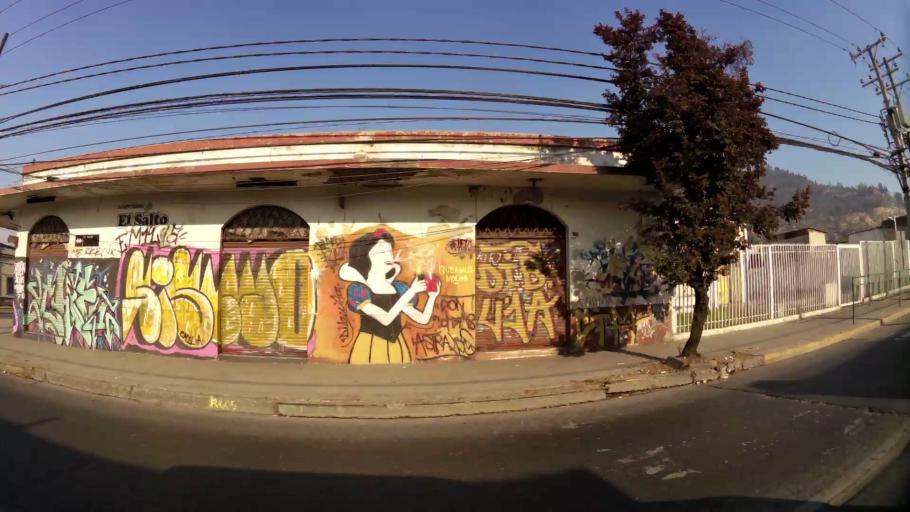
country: CL
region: Santiago Metropolitan
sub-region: Provincia de Santiago
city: Santiago
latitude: -33.4094
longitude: -70.6357
